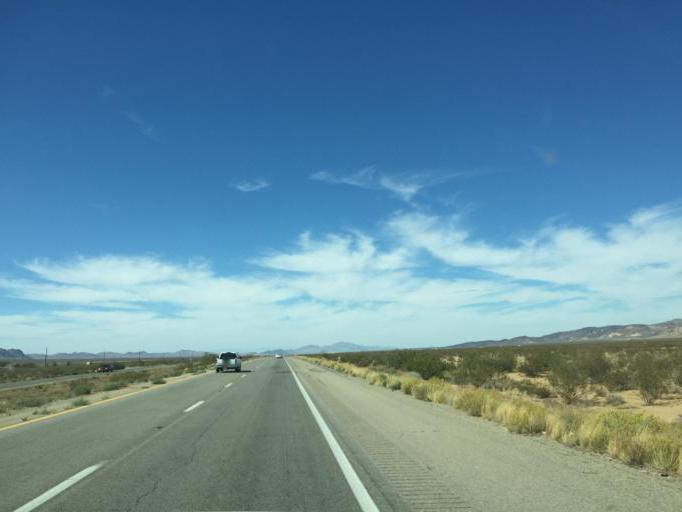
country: US
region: Arizona
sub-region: Mohave County
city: Dolan Springs
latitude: 35.5648
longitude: -114.3765
